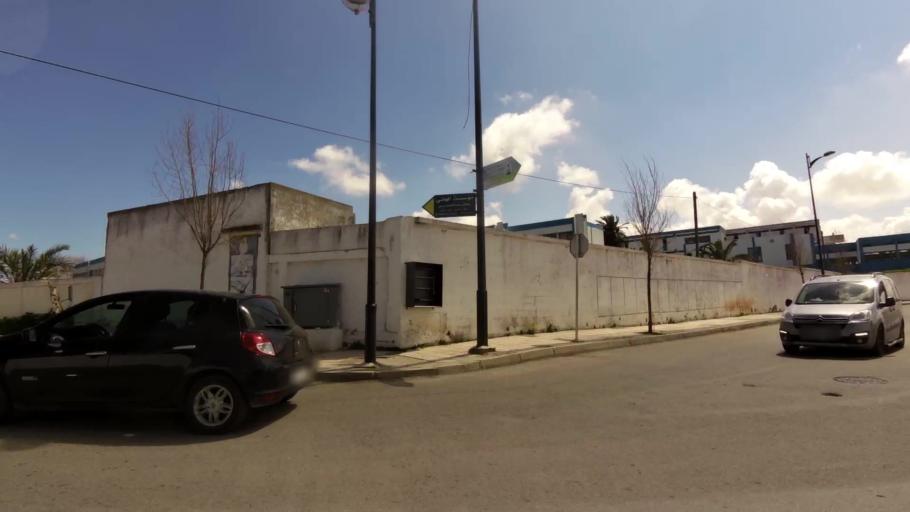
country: MA
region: Tanger-Tetouan
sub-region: Tanger-Assilah
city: Tangier
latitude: 35.7742
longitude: -5.8410
